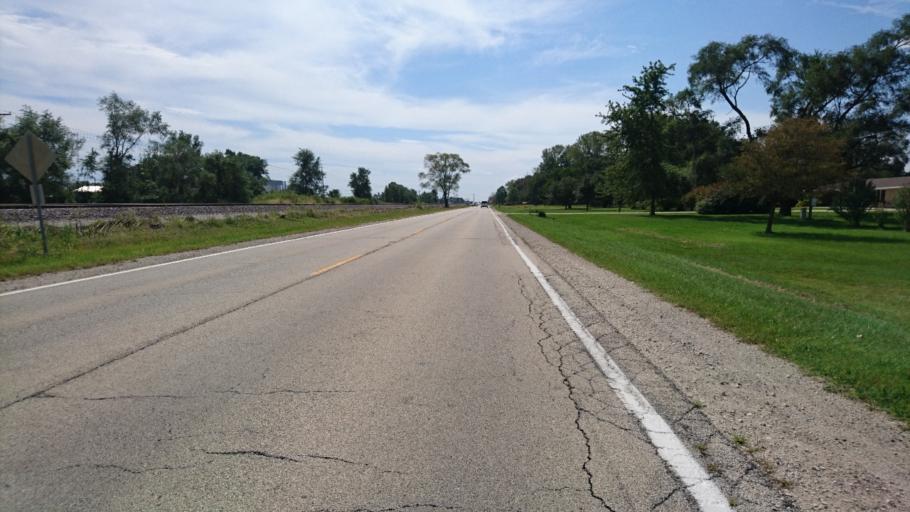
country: US
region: Illinois
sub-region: Will County
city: Braidwood
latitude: 41.2569
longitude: -88.2216
